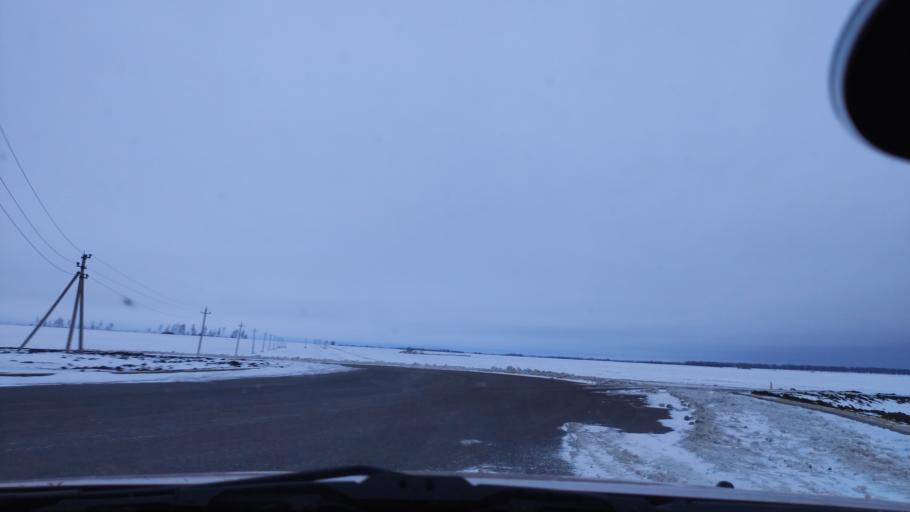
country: RU
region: Tambov
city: Donskoye
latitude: 52.7875
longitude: 41.4287
